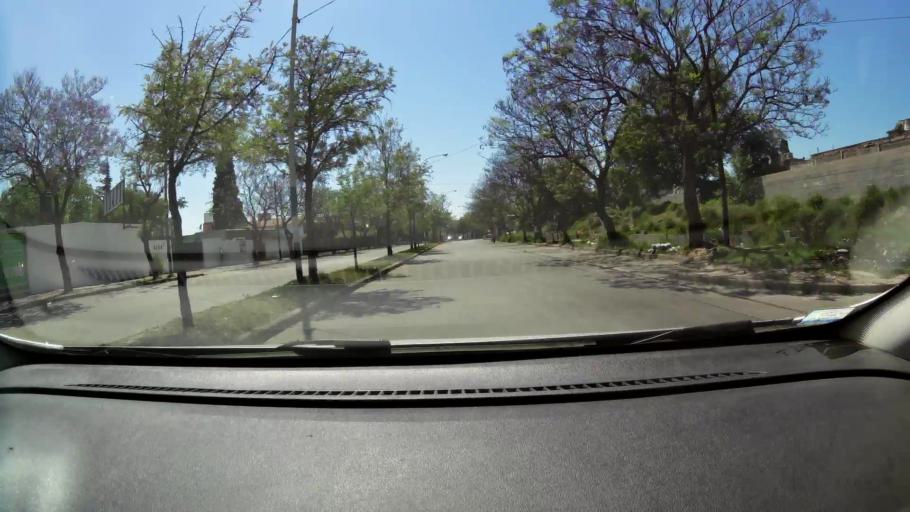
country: AR
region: Cordoba
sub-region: Departamento de Capital
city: Cordoba
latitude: -31.4204
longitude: -64.2136
